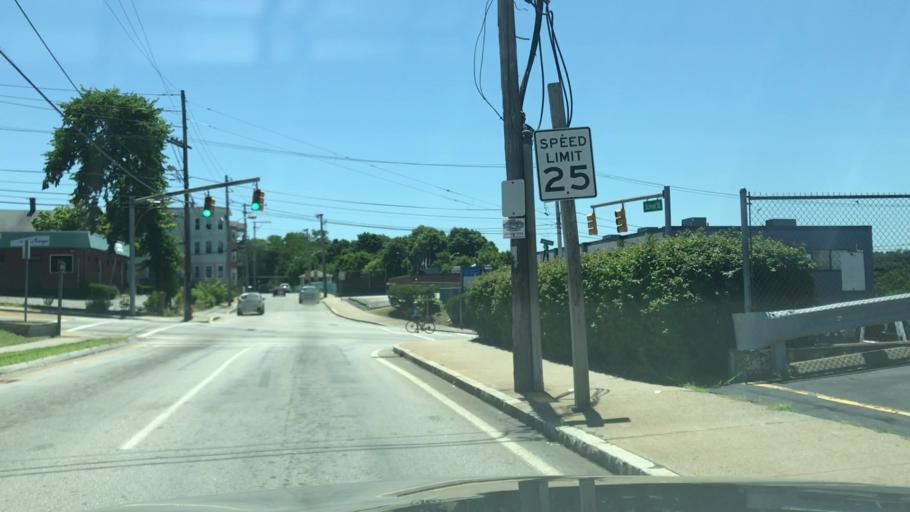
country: US
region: Rhode Island
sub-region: Providence County
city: Pawtucket
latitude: 41.8734
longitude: -71.3809
